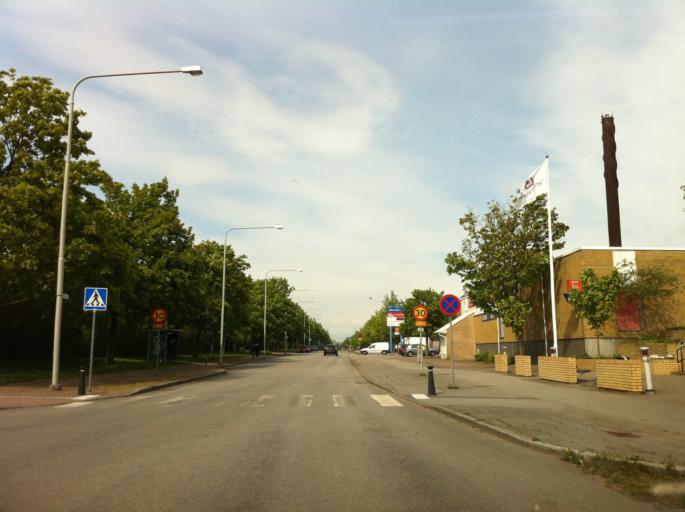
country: SE
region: Skane
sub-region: Landskrona
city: Landskrona
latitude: 55.8881
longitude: 12.8407
